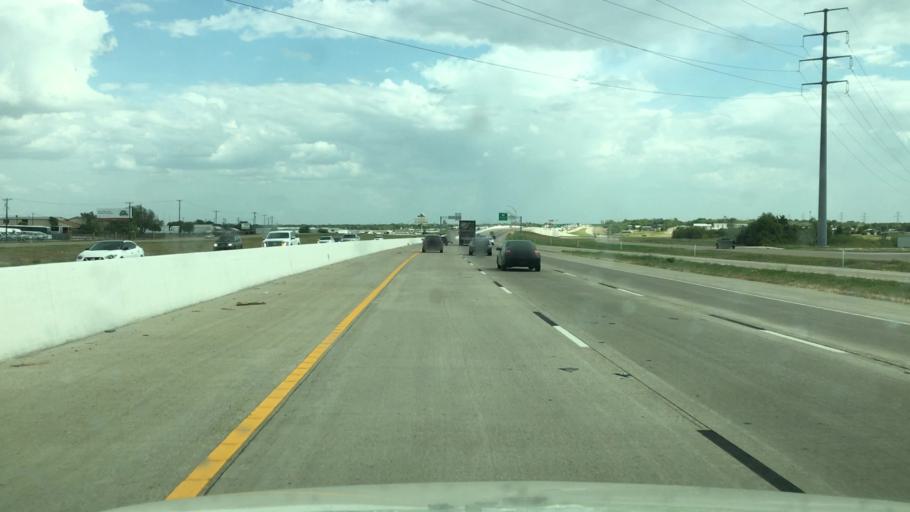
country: US
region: Texas
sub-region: McLennan County
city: Northcrest
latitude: 31.6947
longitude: -97.1010
